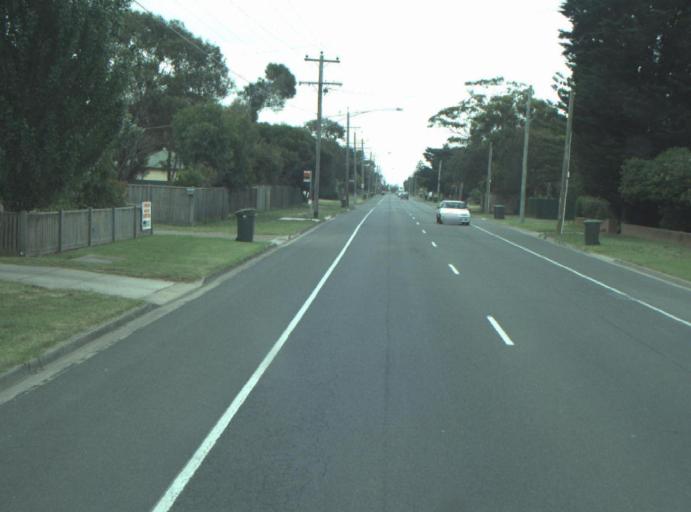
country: AU
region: Victoria
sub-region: Greater Geelong
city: East Geelong
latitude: -38.1711
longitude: 144.4029
